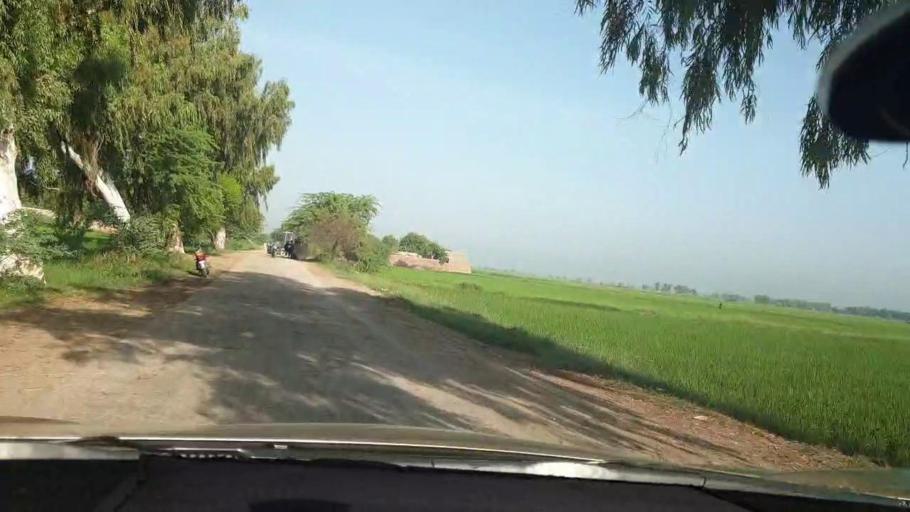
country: PK
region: Sindh
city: Kambar
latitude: 27.6531
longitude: 68.0354
